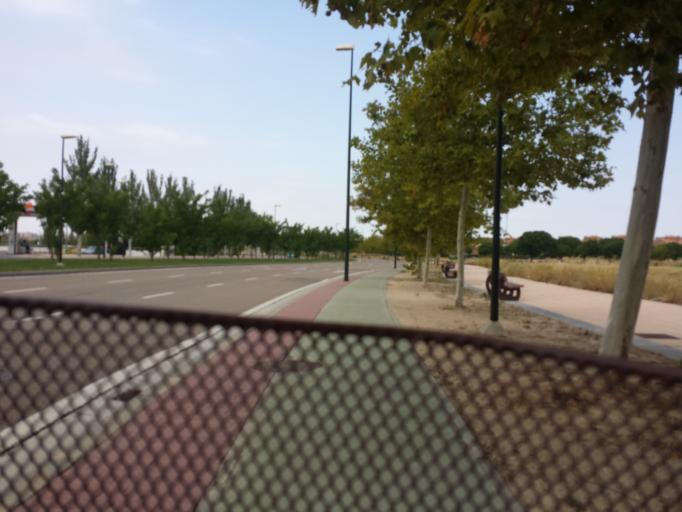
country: ES
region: Aragon
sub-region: Provincia de Zaragoza
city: Montecanal
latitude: 41.6227
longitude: -0.9380
